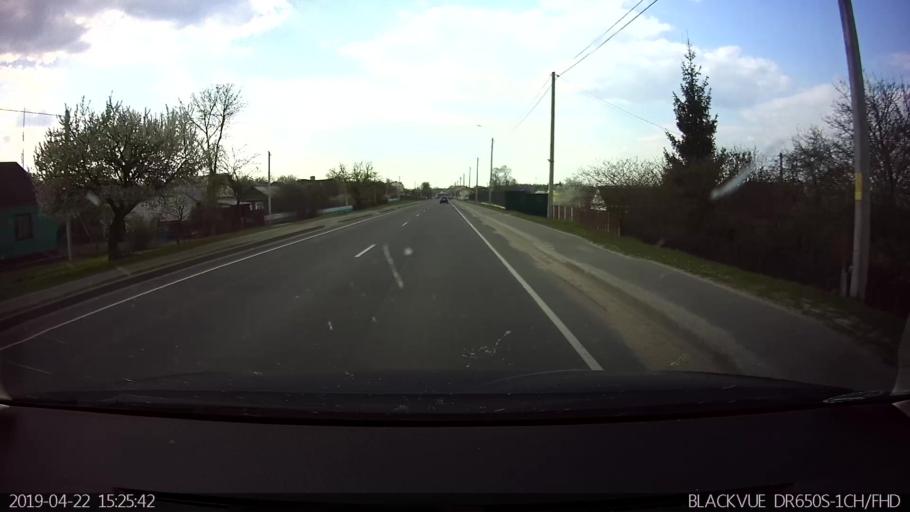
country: BY
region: Brest
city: Vysokaye
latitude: 52.3654
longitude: 23.3925
